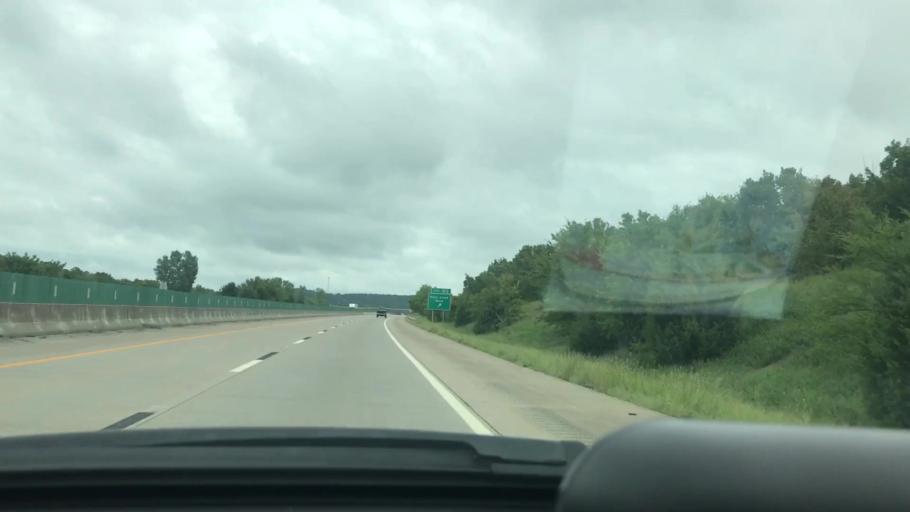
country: US
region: Oklahoma
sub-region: Pittsburg County
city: Krebs
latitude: 35.0947
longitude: -95.6993
